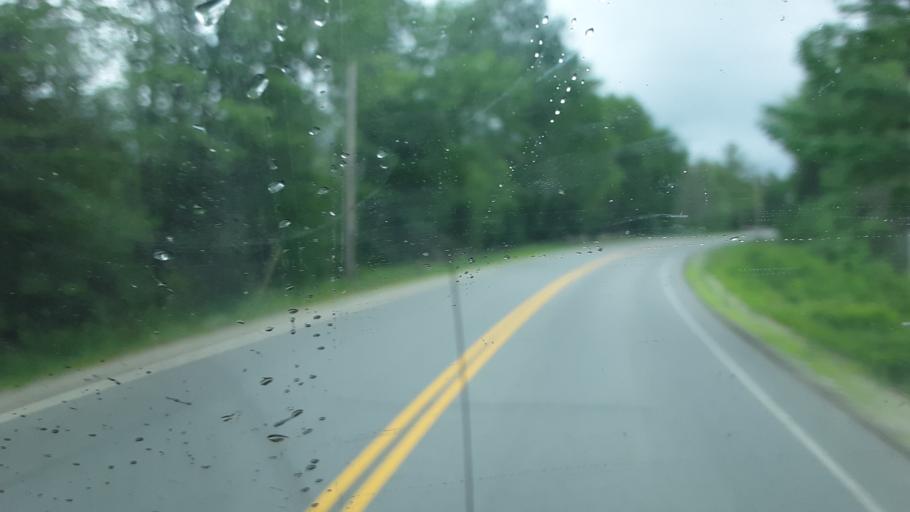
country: US
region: Maine
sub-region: Penobscot County
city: Millinocket
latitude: 45.6864
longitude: -68.7756
